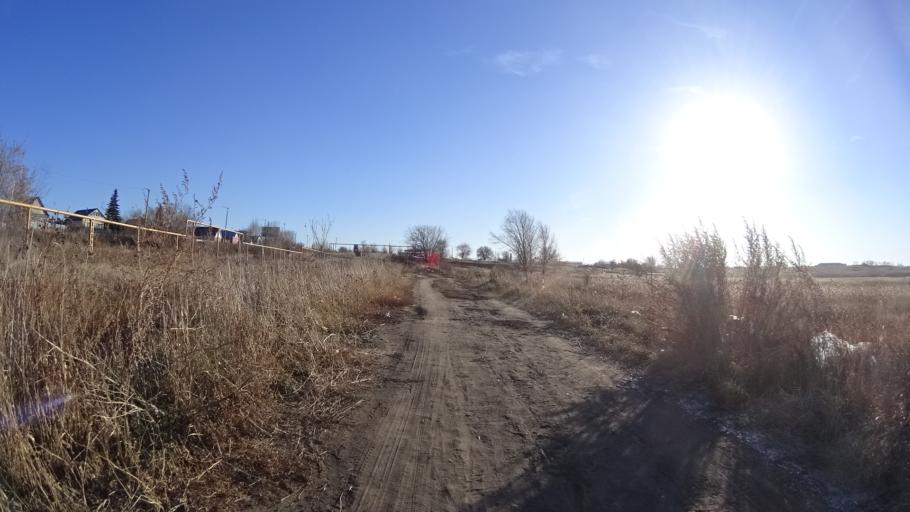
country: RU
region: Chelyabinsk
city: Troitsk
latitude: 54.0855
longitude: 61.5931
